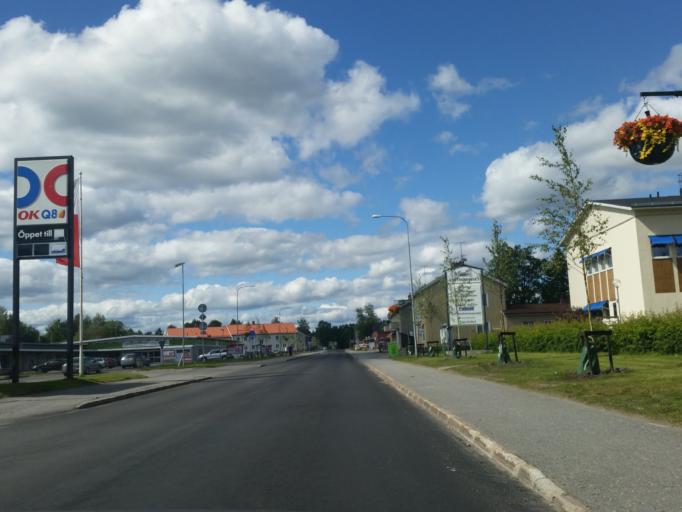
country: SE
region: Vaesterbotten
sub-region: Robertsfors Kommun
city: Robertsfors
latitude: 64.1923
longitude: 20.8500
